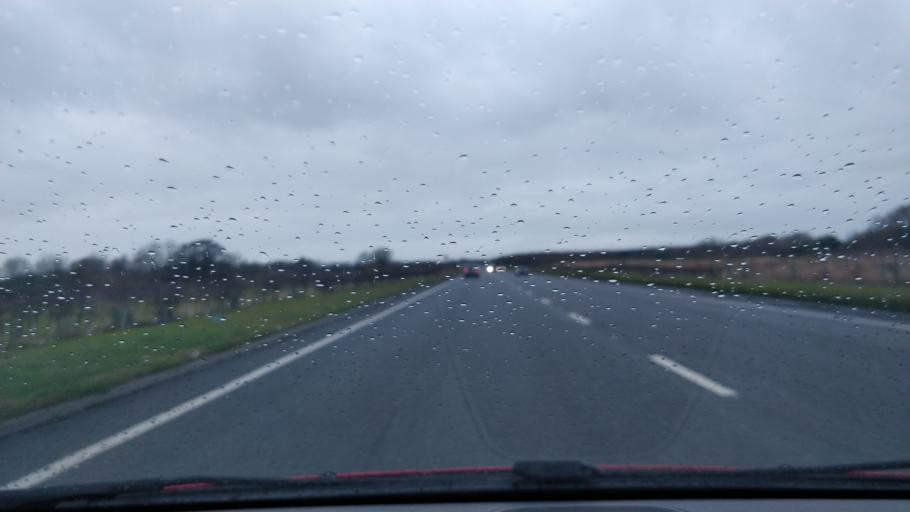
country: GB
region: England
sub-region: Sefton
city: Thornton
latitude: 53.5005
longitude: -2.9869
